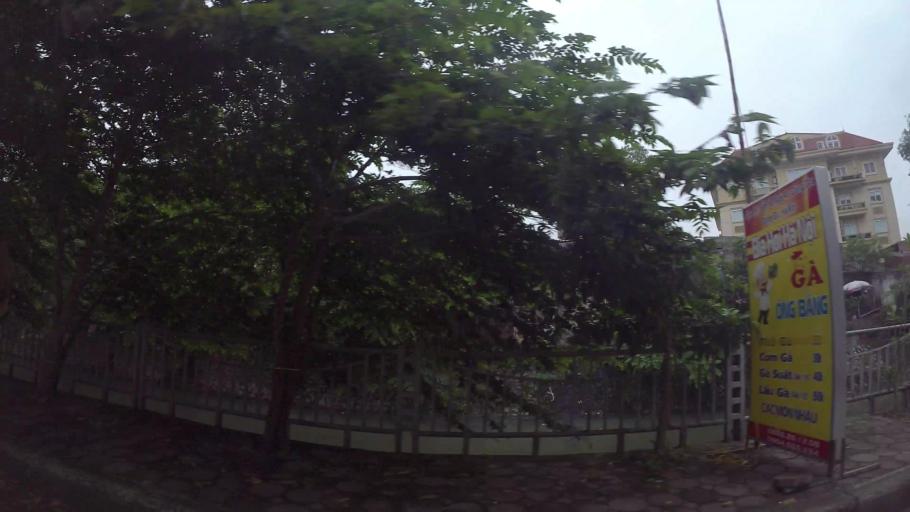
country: VN
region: Ha Noi
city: Dong Da
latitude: 21.0033
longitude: 105.8325
